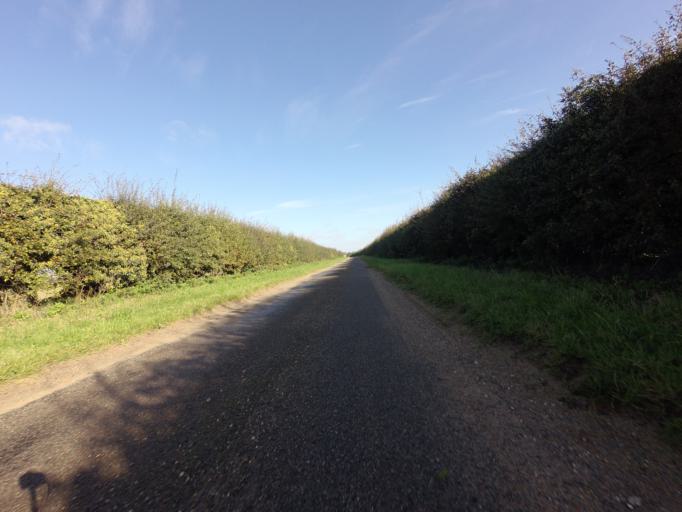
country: GB
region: England
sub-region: Norfolk
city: Dersingham
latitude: 52.8317
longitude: 0.6745
